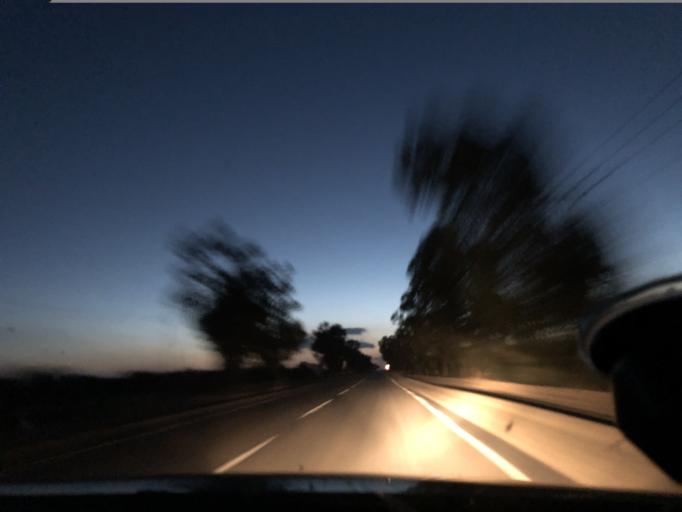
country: TN
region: Al Qasrayn
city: Kasserine
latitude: 35.2522
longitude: 9.0108
